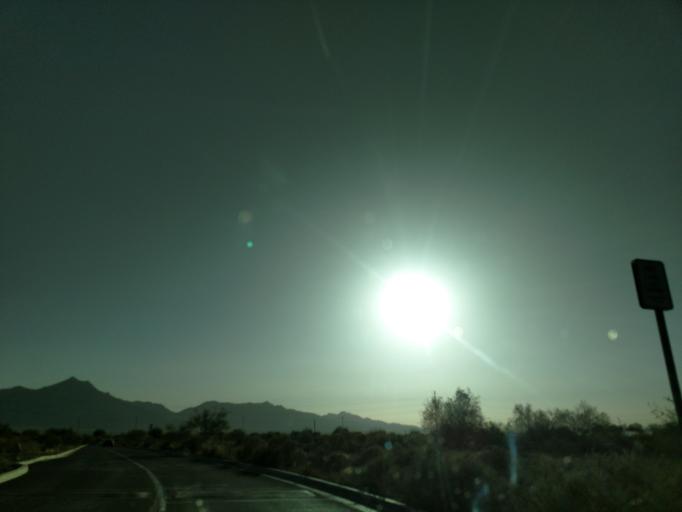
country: US
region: Arizona
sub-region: Maricopa County
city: Laveen
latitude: 33.3121
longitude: -112.1584
